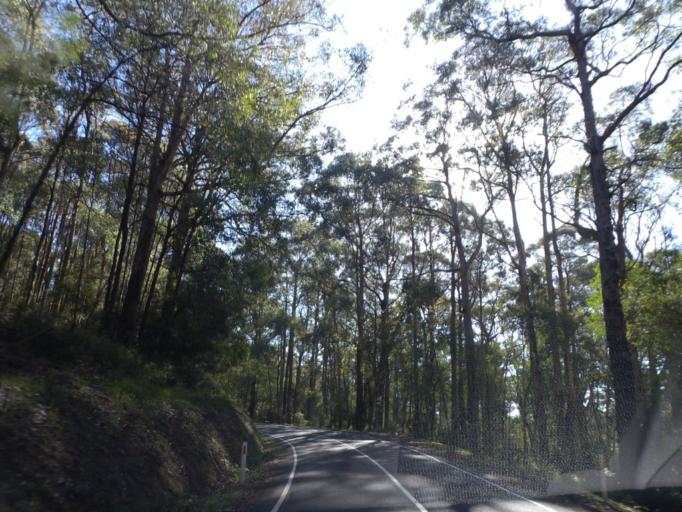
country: AU
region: Victoria
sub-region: Yarra Ranges
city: Millgrove
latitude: -37.8740
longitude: 145.7954
